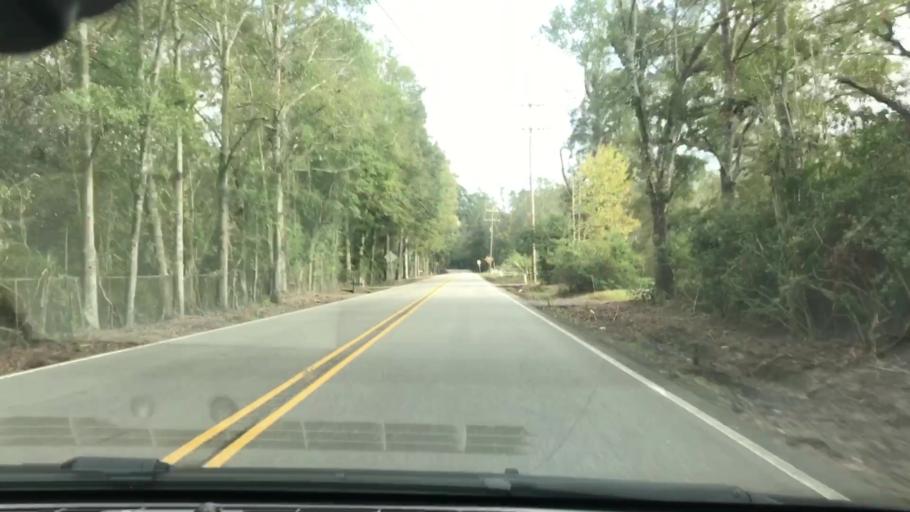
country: US
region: Louisiana
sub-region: Saint Tammany Parish
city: Abita Springs
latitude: 30.5339
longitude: -89.8847
